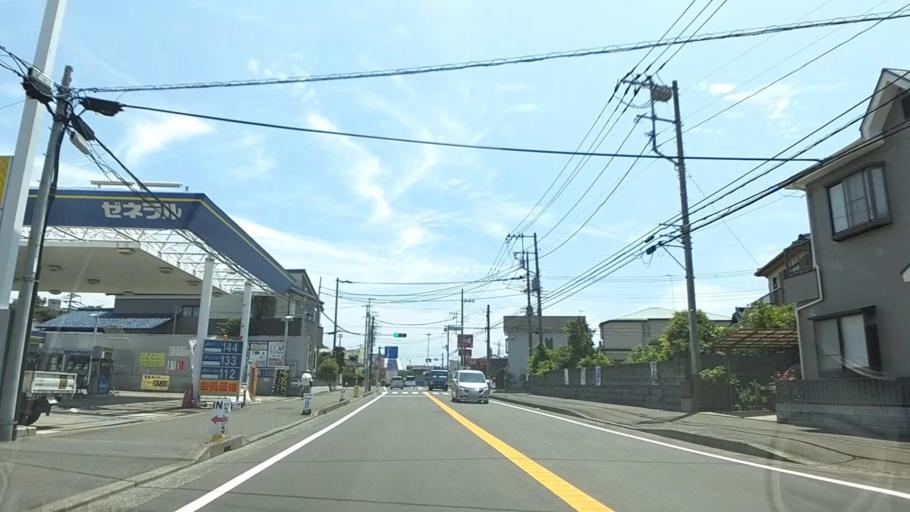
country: JP
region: Kanagawa
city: Atsugi
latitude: 35.3866
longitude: 139.3812
